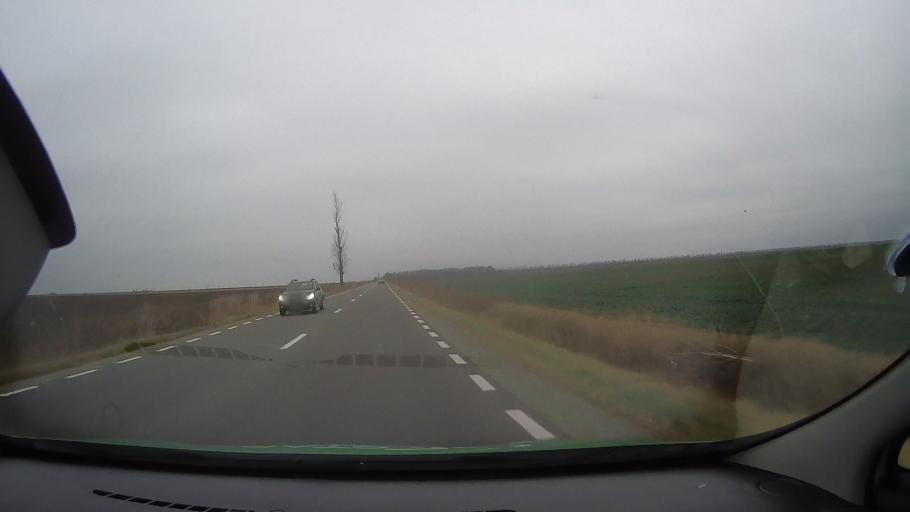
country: RO
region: Ialomita
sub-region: Comuna Scanteia
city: Iazu
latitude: 44.7092
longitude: 27.4191
